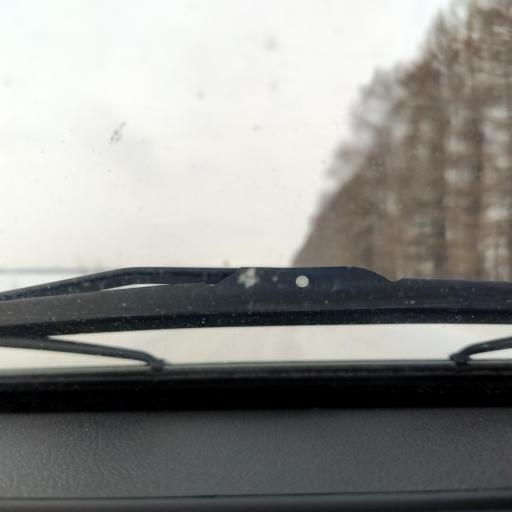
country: RU
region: Bashkortostan
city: Mikhaylovka
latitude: 54.8541
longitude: 55.8707
